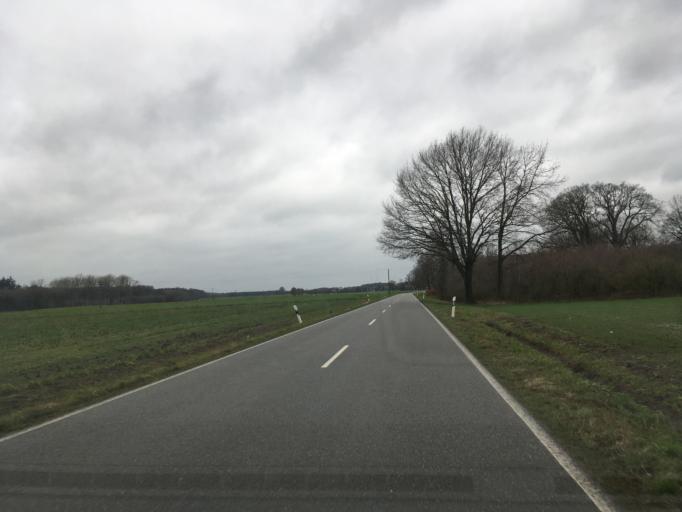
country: DE
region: North Rhine-Westphalia
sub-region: Regierungsbezirk Munster
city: Legden
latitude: 52.0460
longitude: 7.1643
